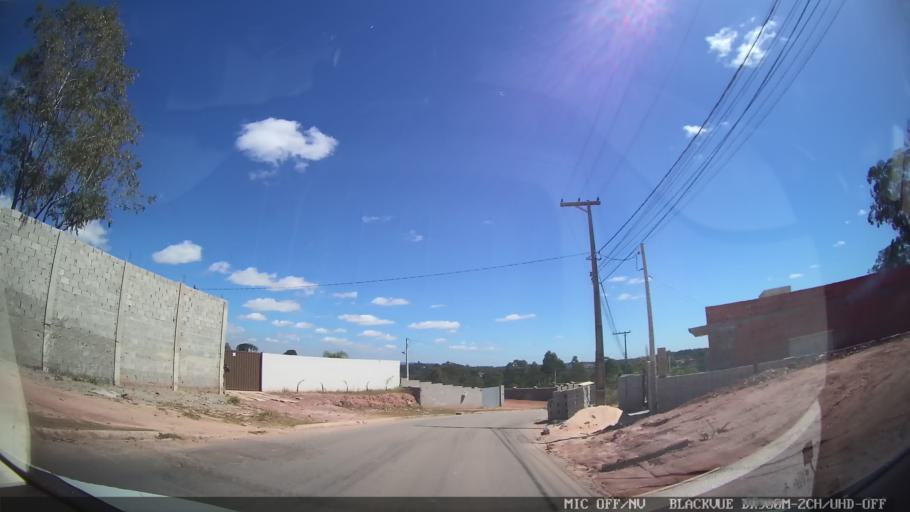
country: BR
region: Sao Paulo
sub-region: Campo Limpo Paulista
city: Campo Limpo Paulista
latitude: -23.1805
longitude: -46.7441
